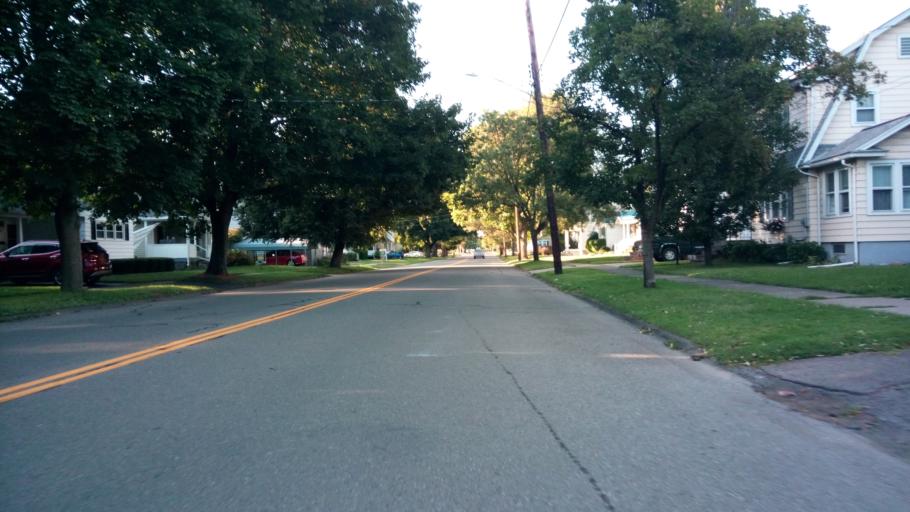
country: US
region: New York
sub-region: Chemung County
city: Elmira Heights
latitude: 42.1122
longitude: -76.8265
